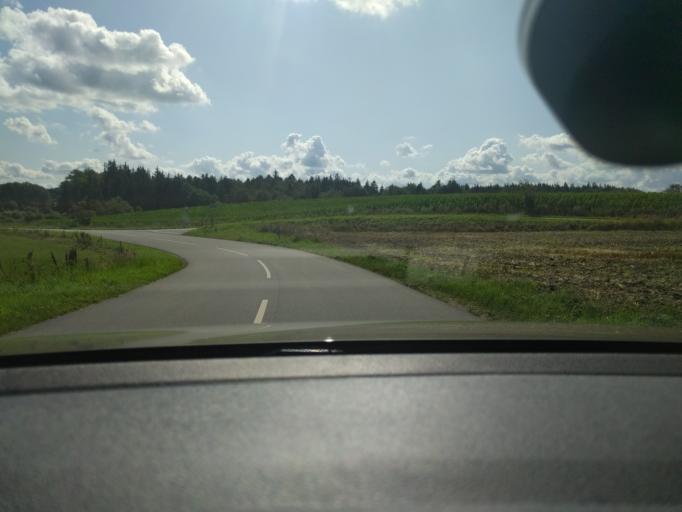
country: DK
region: Central Jutland
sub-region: Viborg Kommune
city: Bjerringbro
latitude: 56.5115
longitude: 9.5777
